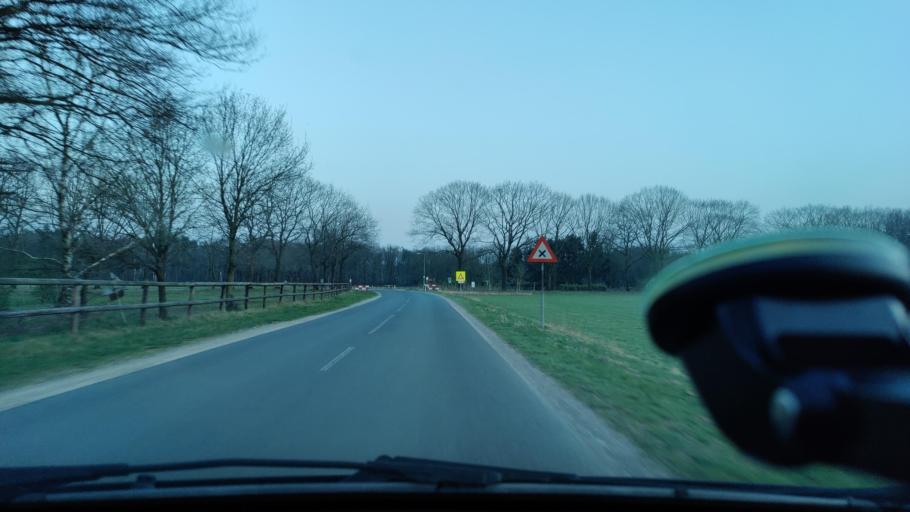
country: NL
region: Limburg
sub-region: Gemeente Venlo
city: Arcen
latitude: 51.5274
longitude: 6.1898
